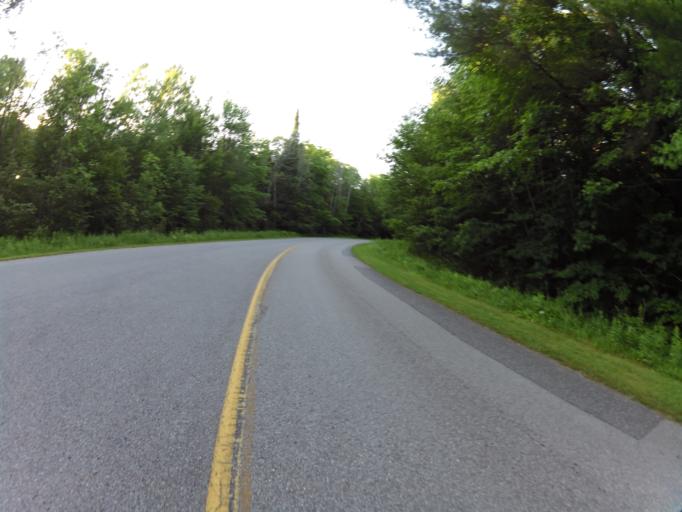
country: CA
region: Quebec
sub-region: Outaouais
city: Wakefield
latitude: 45.6076
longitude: -76.0133
